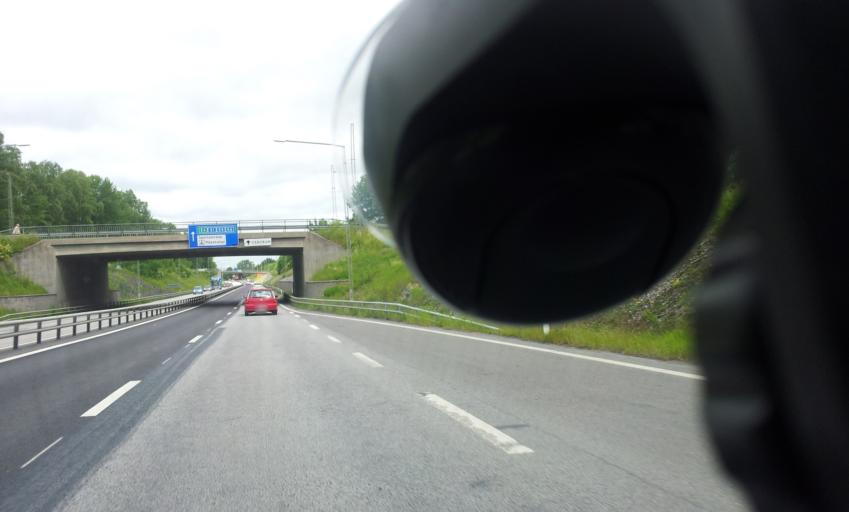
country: SE
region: OEstergoetland
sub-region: Norrkopings Kommun
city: Norrkoping
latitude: 58.5792
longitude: 16.1571
